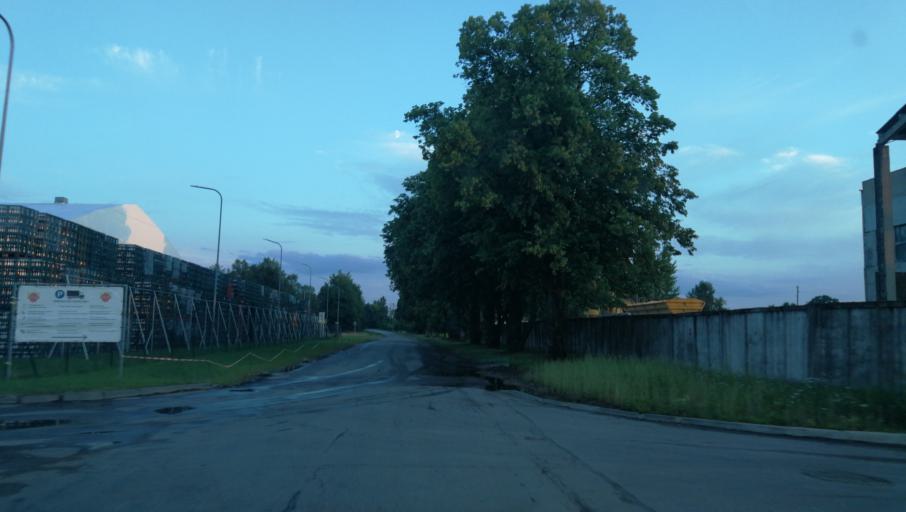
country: LV
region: Cesu Rajons
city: Cesis
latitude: 57.3184
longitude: 25.3030
